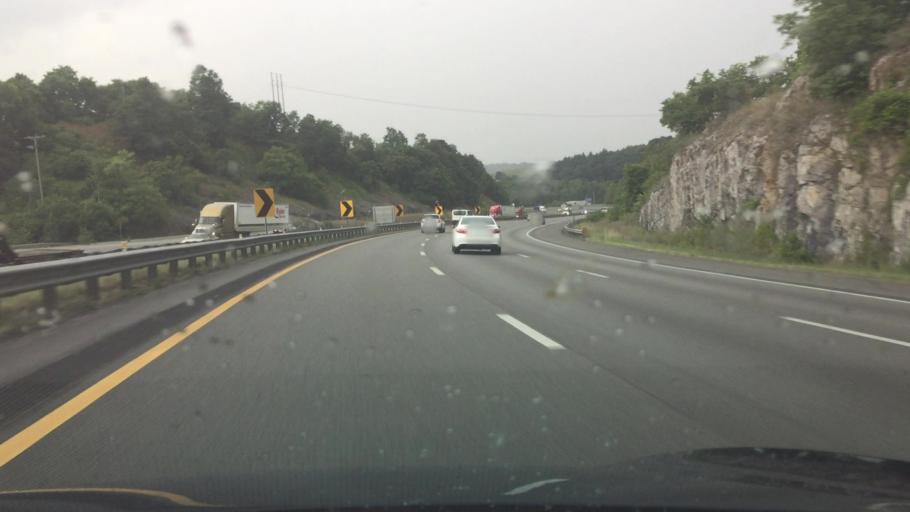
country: US
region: Virginia
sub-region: Wythe County
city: Wytheville
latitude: 36.9415
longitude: -81.0229
